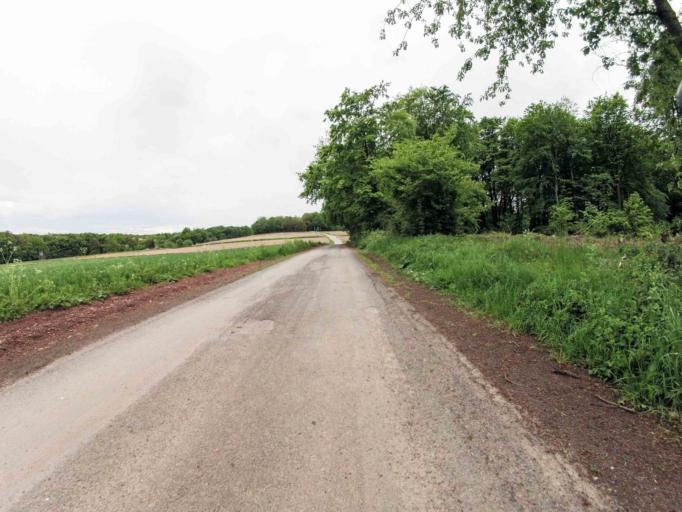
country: DE
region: Lower Saxony
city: Bad Essen
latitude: 52.2791
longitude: 8.2942
